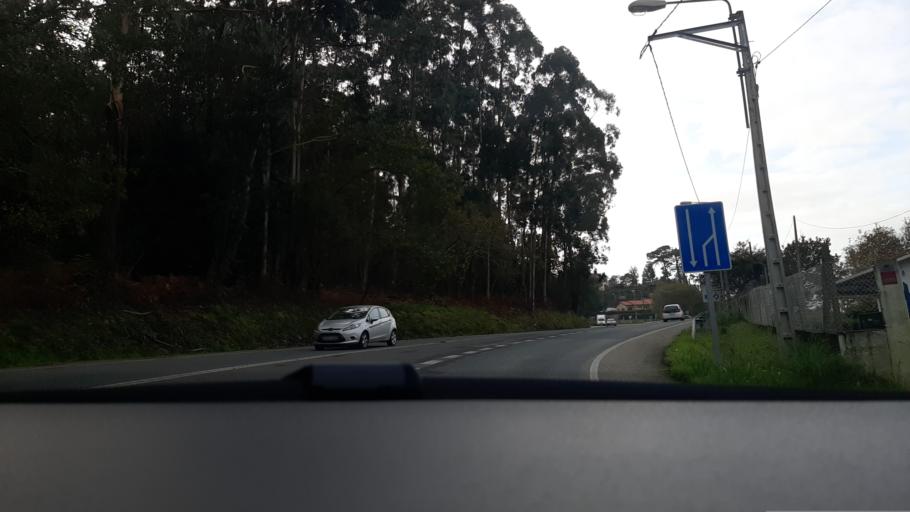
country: ES
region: Galicia
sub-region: Provincia de Pontevedra
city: Nigran
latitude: 42.1803
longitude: -8.7930
